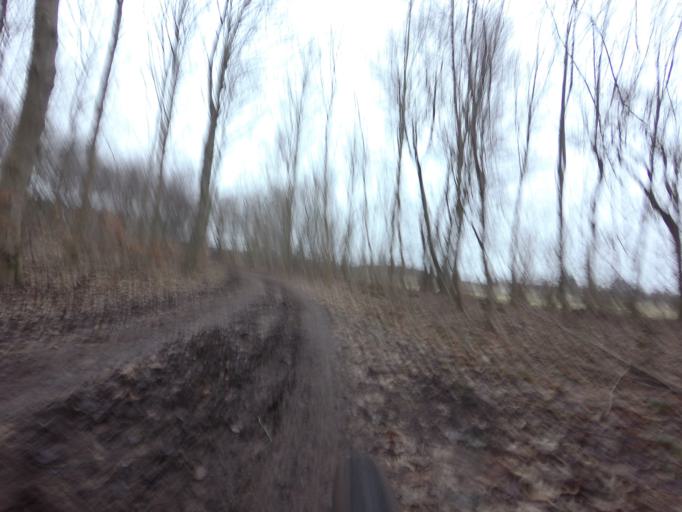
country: DK
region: Central Jutland
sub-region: Arhus Kommune
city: Stavtrup
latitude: 56.1394
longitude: 10.1065
